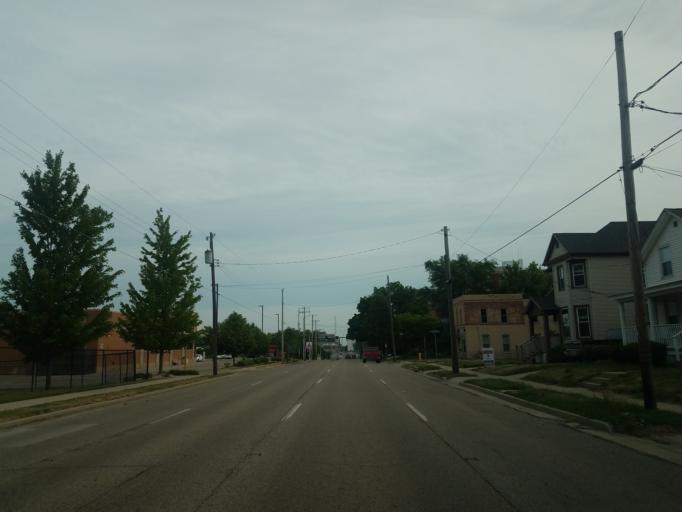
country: US
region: Illinois
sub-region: McLean County
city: Bloomington
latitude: 40.4701
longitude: -88.9932
